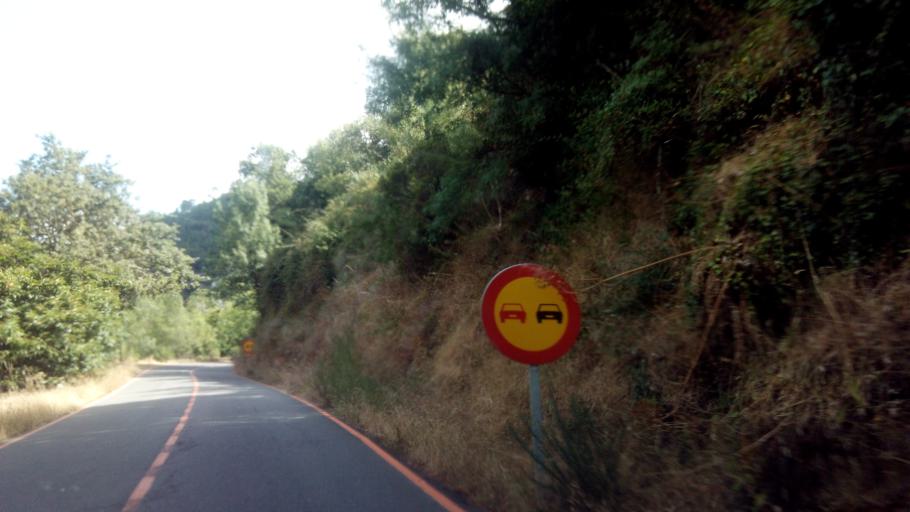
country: ES
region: Galicia
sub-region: Provincia de Ourense
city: Nogueira de Ramuin
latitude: 42.4500
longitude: -7.7334
